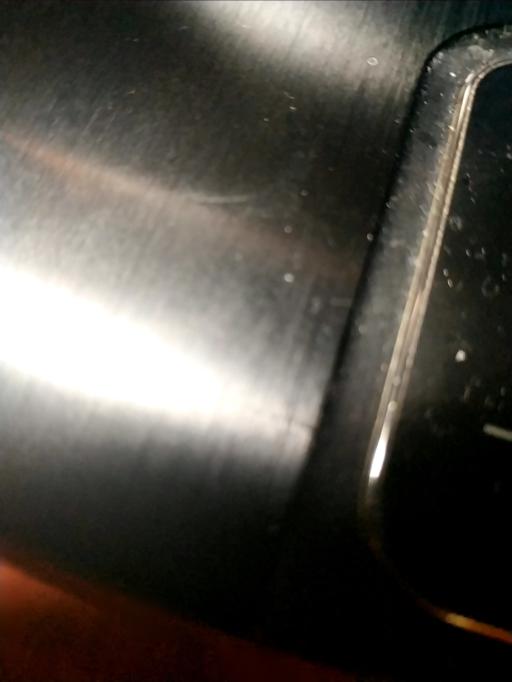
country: RU
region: Republic of Karelia
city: Belomorsk
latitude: 64.3402
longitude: 34.9102
